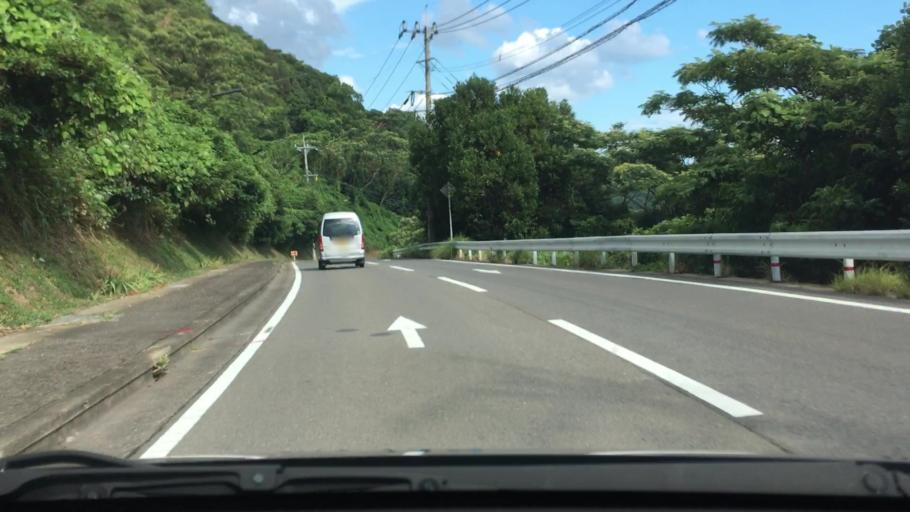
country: JP
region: Nagasaki
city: Togitsu
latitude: 32.8497
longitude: 129.6912
